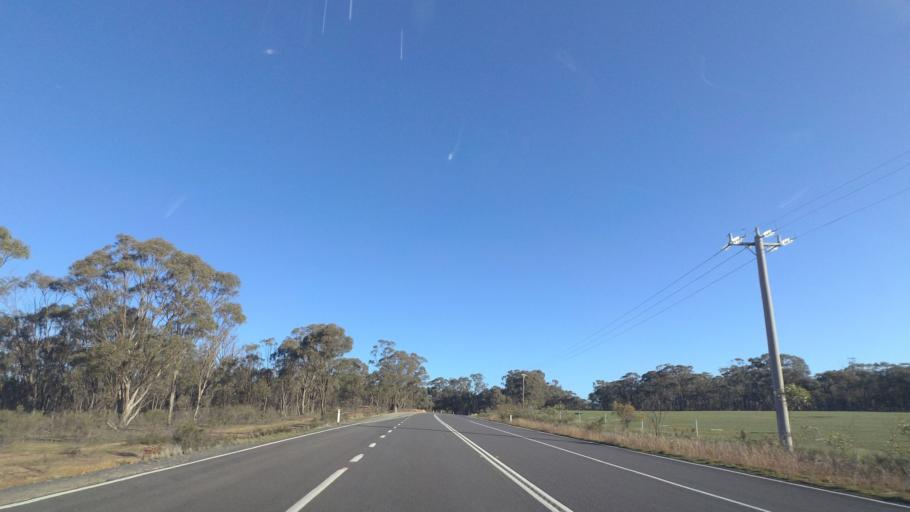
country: AU
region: Victoria
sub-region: Greater Bendigo
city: Kennington
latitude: -36.8719
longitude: 144.4985
